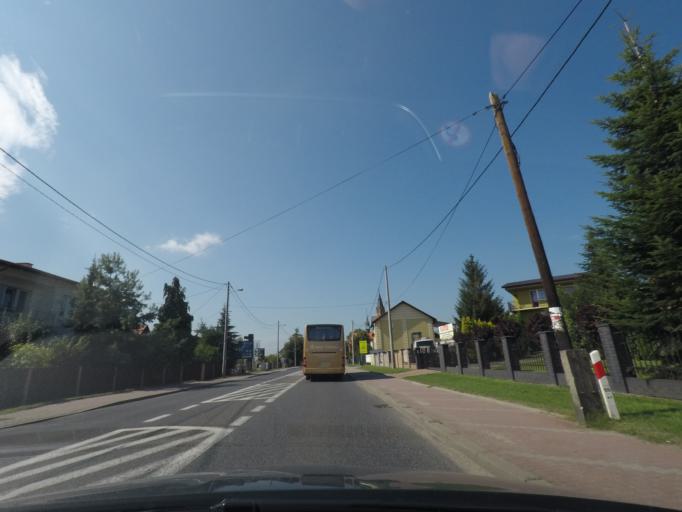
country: PL
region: Lesser Poland Voivodeship
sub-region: Powiat chrzanowski
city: Libiaz
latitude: 50.1016
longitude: 19.3117
